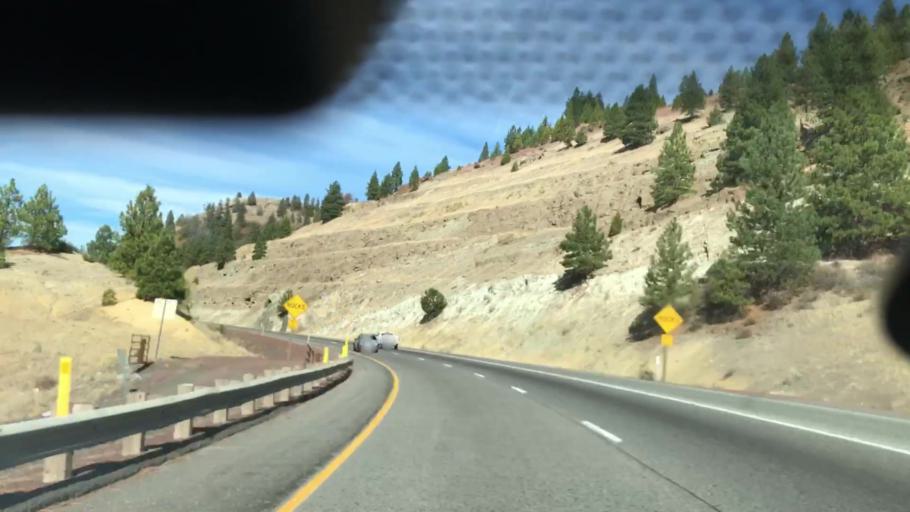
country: US
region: Oregon
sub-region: Jackson County
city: Ashland
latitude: 42.0399
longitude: -122.5979
